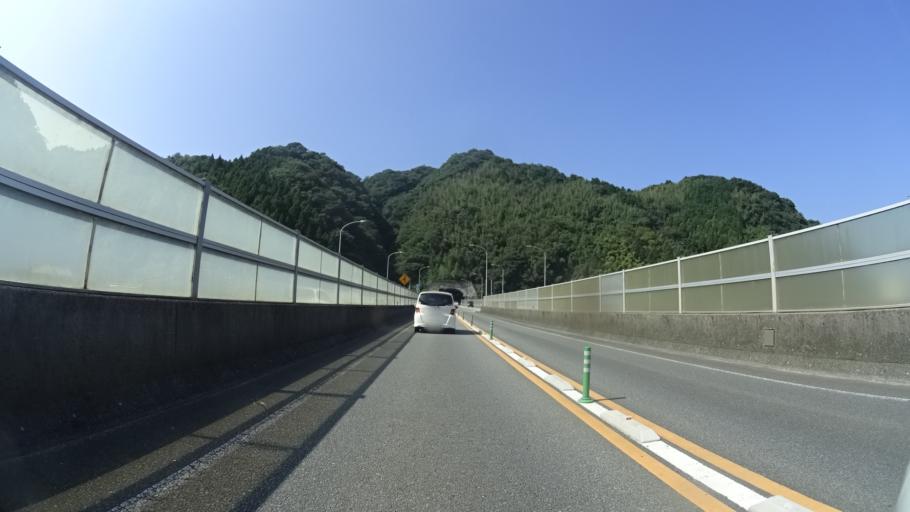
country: JP
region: Shimane
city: Hamada
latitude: 34.8942
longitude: 132.1028
